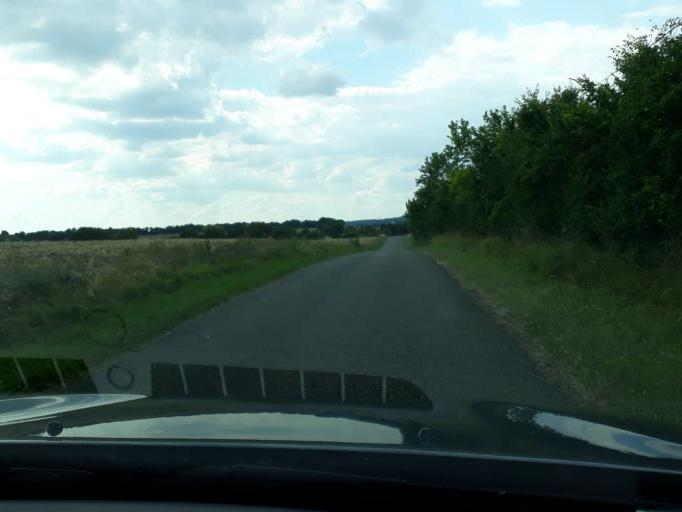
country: FR
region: Centre
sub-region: Departement du Cher
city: Jouet-sur-l'Aubois
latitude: 46.9830
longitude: 2.9291
